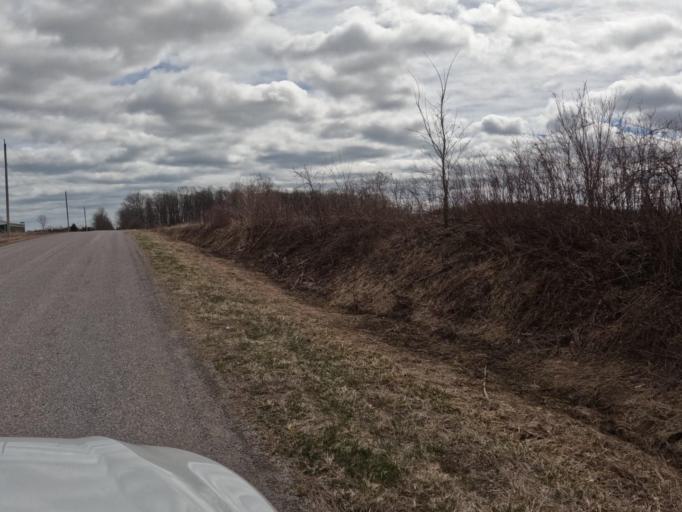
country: CA
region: Ontario
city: Norfolk County
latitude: 42.8520
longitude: -80.1707
